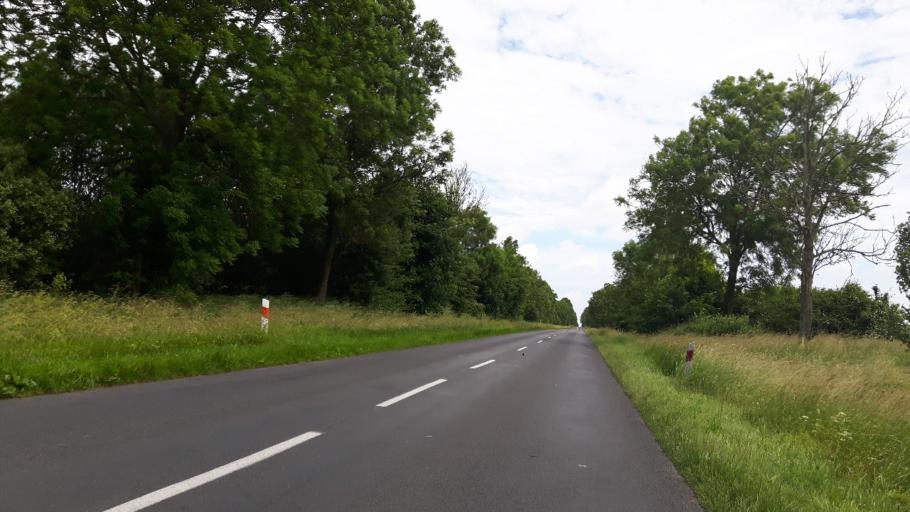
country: PL
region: West Pomeranian Voivodeship
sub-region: Powiat gryficki
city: Trzebiatow
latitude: 54.0310
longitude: 15.2416
